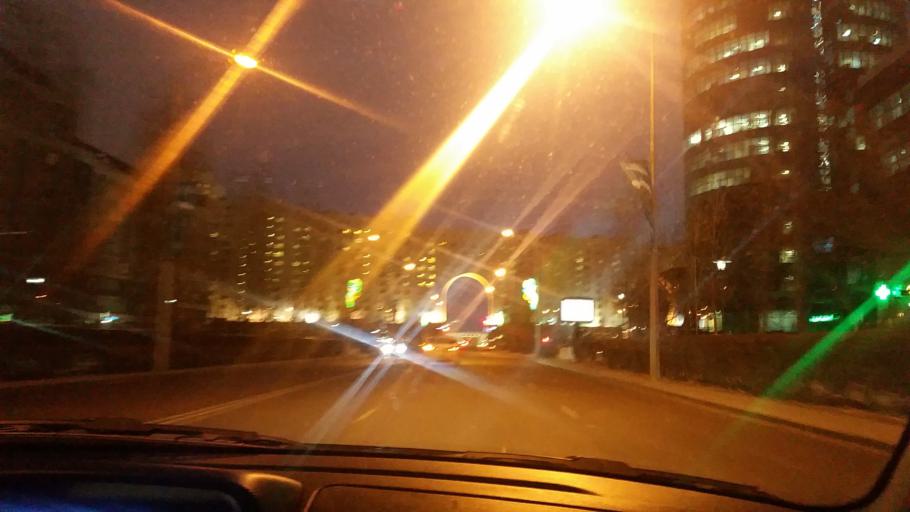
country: KZ
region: Astana Qalasy
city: Astana
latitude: 51.1251
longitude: 71.4345
